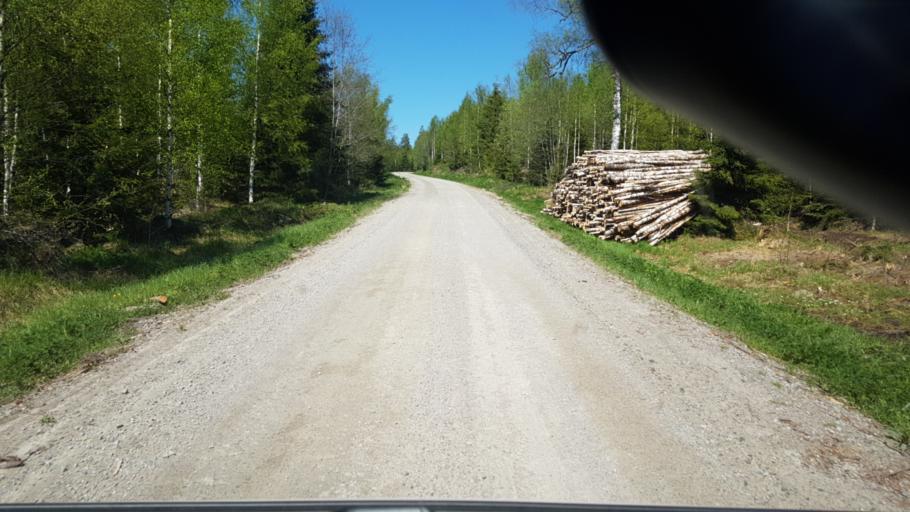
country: SE
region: Vaermland
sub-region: Arvika Kommun
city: Arvika
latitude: 59.8191
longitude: 12.7441
